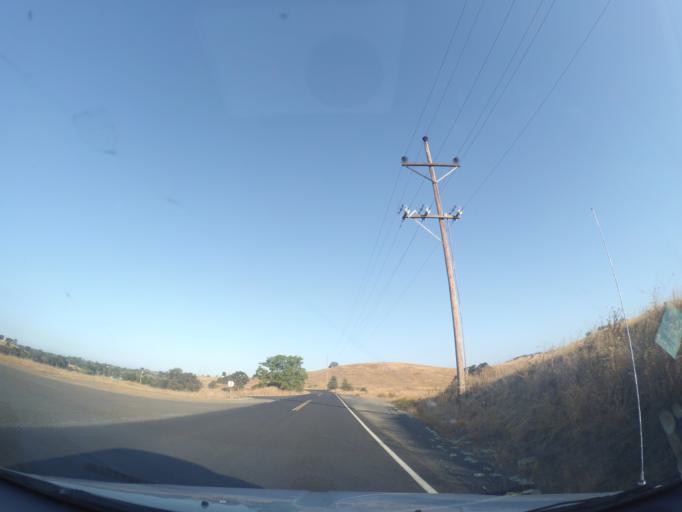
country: US
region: California
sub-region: Merced County
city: Planada
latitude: 37.5240
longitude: -120.3115
